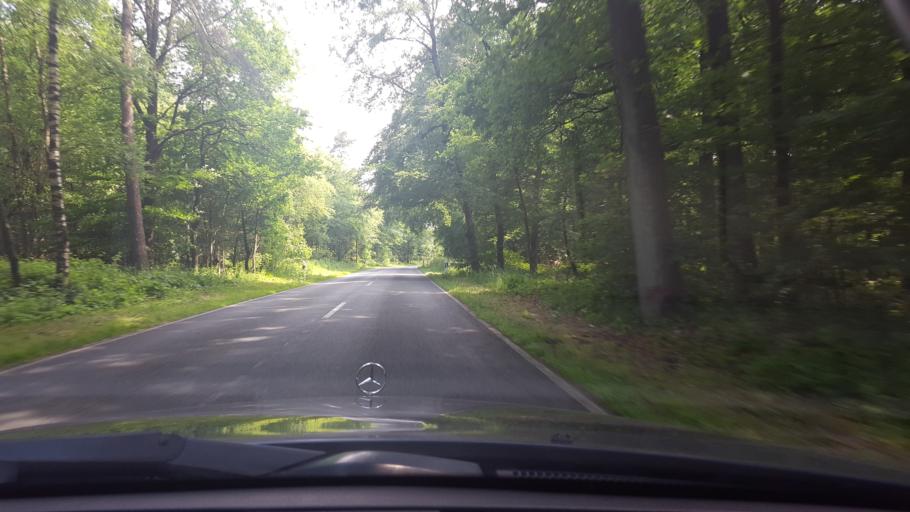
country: DE
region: North Rhine-Westphalia
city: Olfen
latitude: 51.7199
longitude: 7.3052
